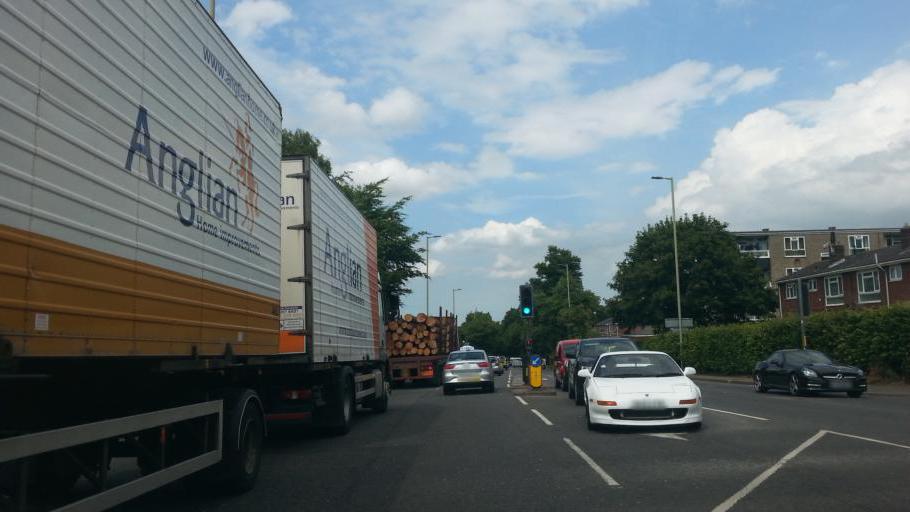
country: GB
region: England
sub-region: Norfolk
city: Cringleford
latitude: 52.6327
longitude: 1.2593
